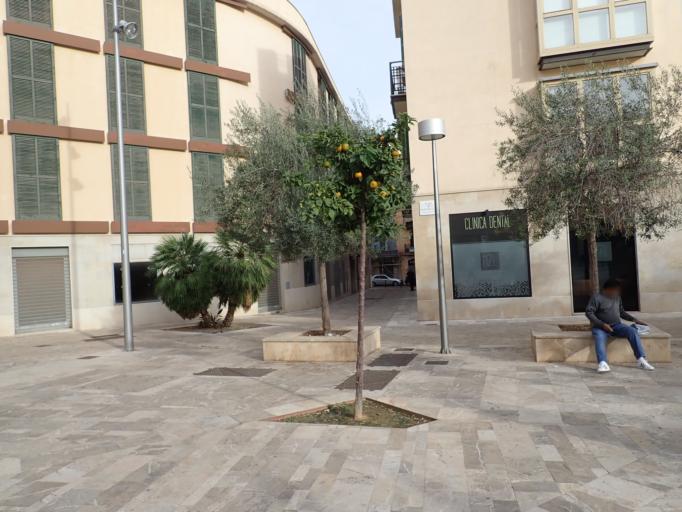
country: ES
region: Balearic Islands
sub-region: Illes Balears
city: Palma
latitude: 39.5709
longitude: 2.6548
